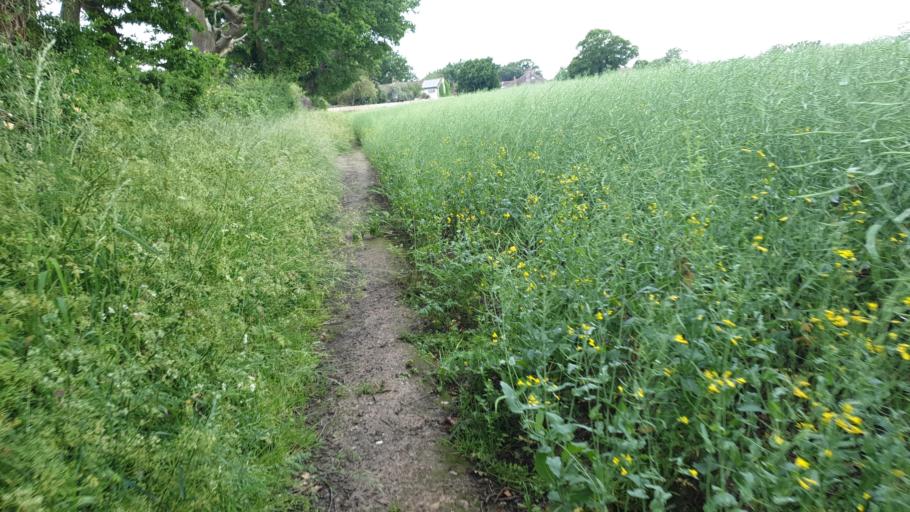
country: GB
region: England
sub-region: Essex
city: Great Bentley
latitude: 51.8851
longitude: 1.1034
